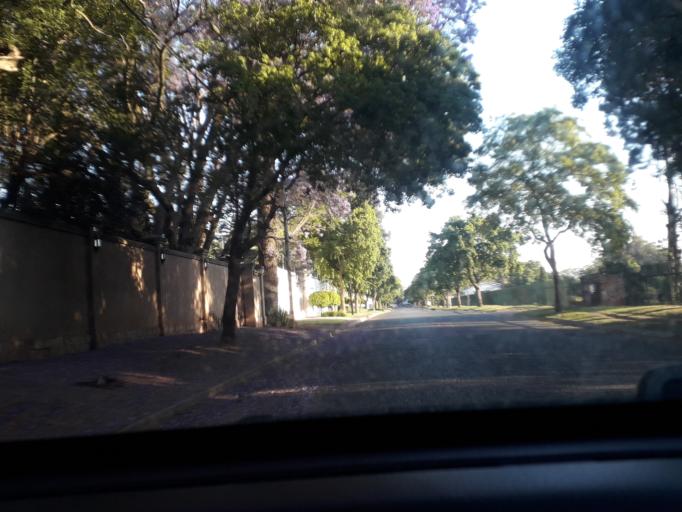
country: ZA
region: Gauteng
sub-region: City of Johannesburg Metropolitan Municipality
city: Johannesburg
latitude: -26.1513
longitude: 28.0537
